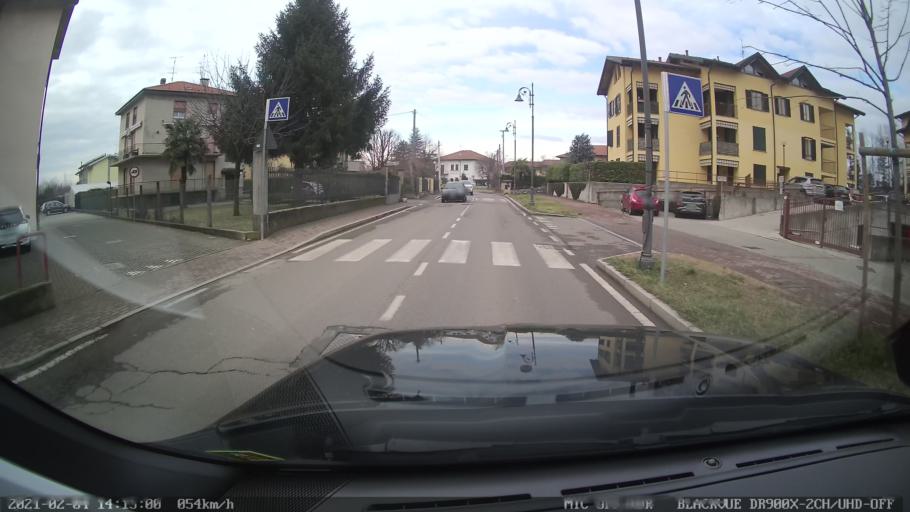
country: IT
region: Lombardy
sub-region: Provincia di Varese
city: Lonate Ceppino
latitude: 45.7216
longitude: 8.8884
